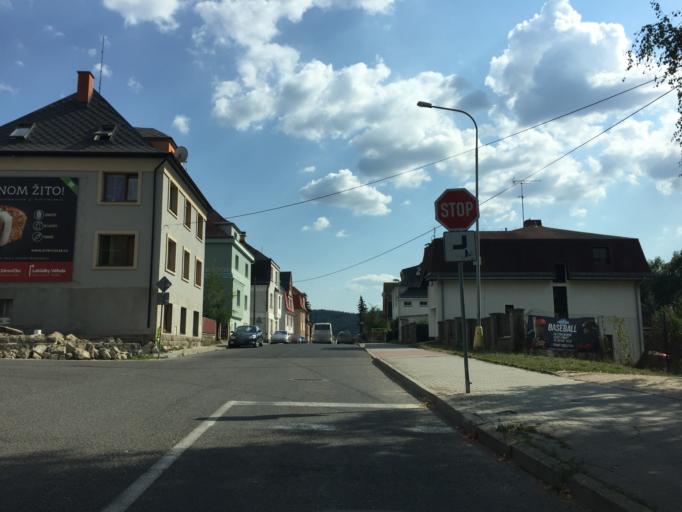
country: CZ
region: Liberecky
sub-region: Okres Jablonec nad Nisou
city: Jablonec nad Nisou
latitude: 50.7314
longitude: 15.1784
